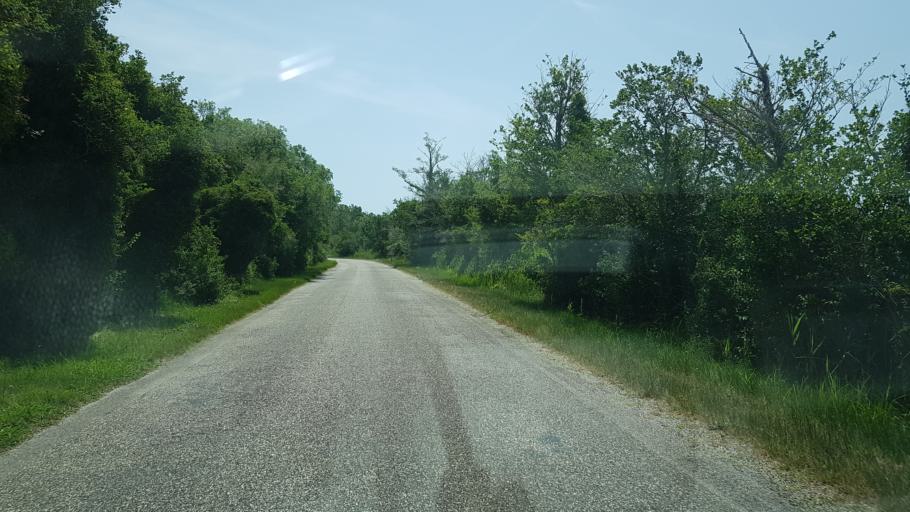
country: FR
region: Provence-Alpes-Cote d'Azur
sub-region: Departement des Bouches-du-Rhone
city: Port-Saint-Louis-du-Rhone
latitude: 43.4588
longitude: 4.6590
